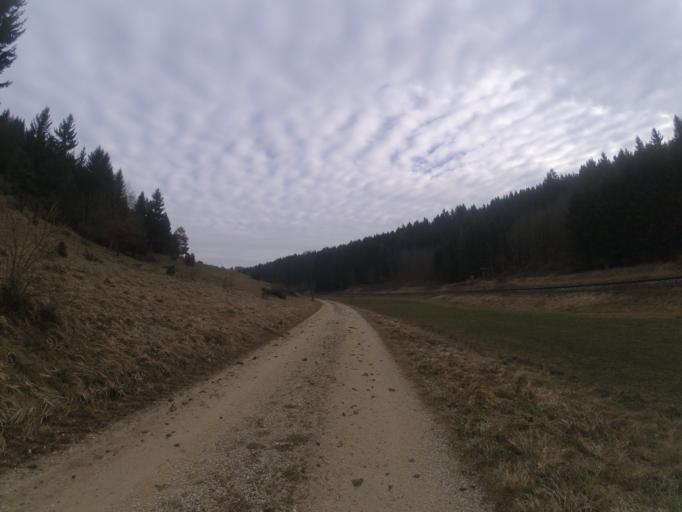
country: DE
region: Baden-Wuerttemberg
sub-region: Tuebingen Region
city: Mehrstetten
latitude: 48.3557
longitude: 9.5482
